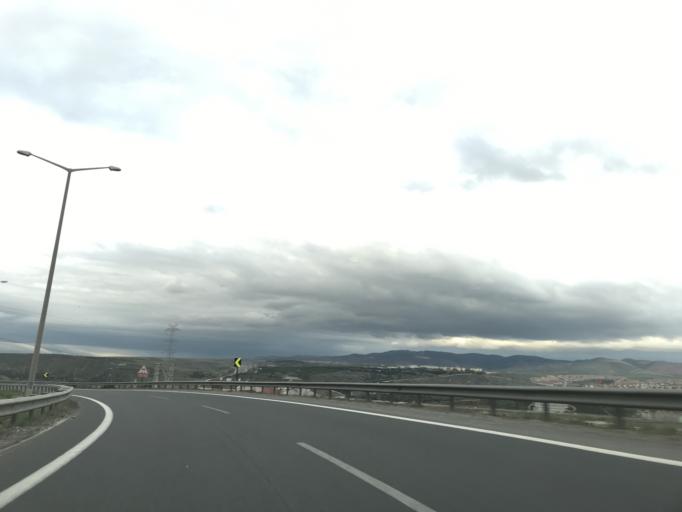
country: TR
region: Ankara
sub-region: Goelbasi
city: Golbasi
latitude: 39.8062
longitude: 32.7992
